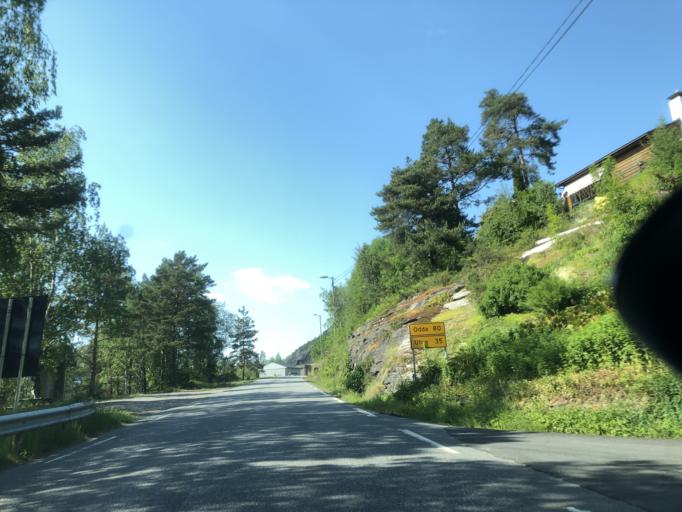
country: NO
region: Hordaland
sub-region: Jondal
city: Jondal
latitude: 60.2832
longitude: 6.2472
